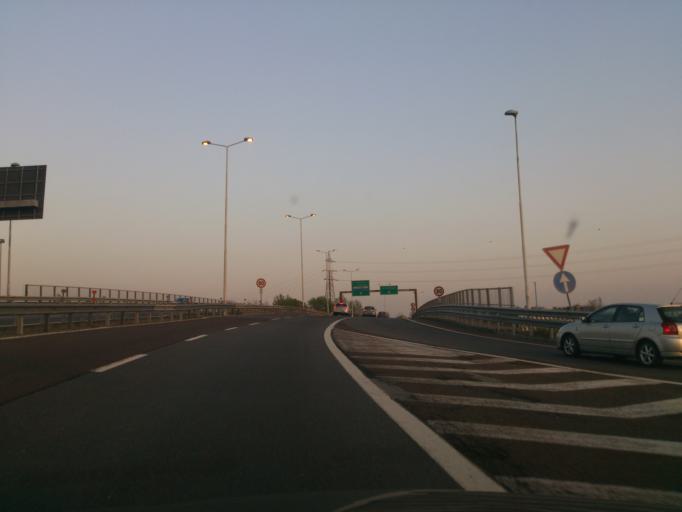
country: IT
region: Lombardy
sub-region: Provincia di Monza e Brianza
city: Monza
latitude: 45.5564
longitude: 9.2653
